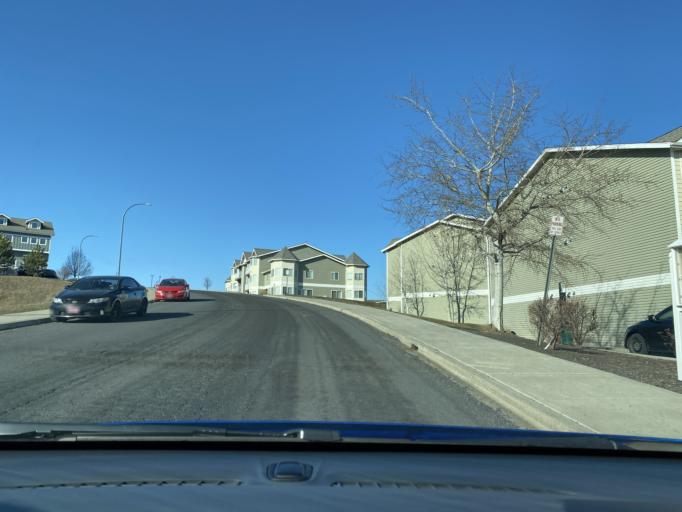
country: US
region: Washington
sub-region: Whitman County
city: Pullman
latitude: 46.7486
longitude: -117.1495
